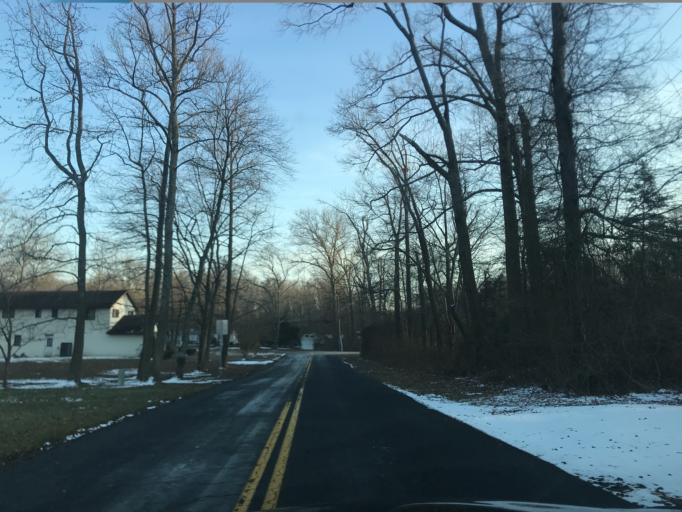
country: US
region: Maryland
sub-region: Harford County
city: Riverside
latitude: 39.4362
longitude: -76.2552
